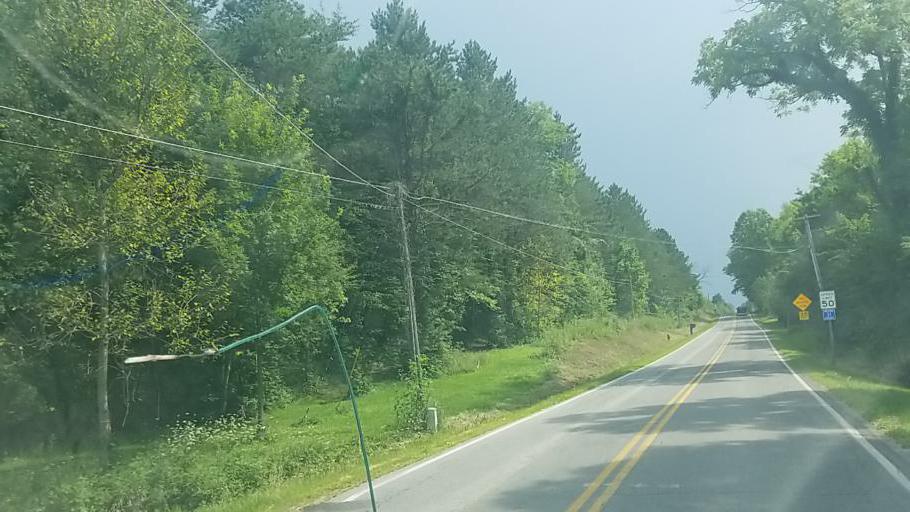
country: US
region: Ohio
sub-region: Medina County
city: Lodi
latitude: 41.0535
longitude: -82.0055
